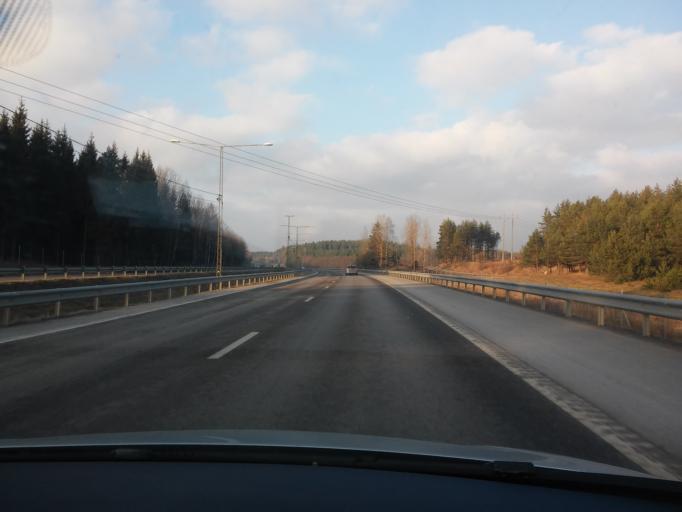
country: SE
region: Stockholm
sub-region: Taby Kommun
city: Taby
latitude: 59.4763
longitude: 18.1633
